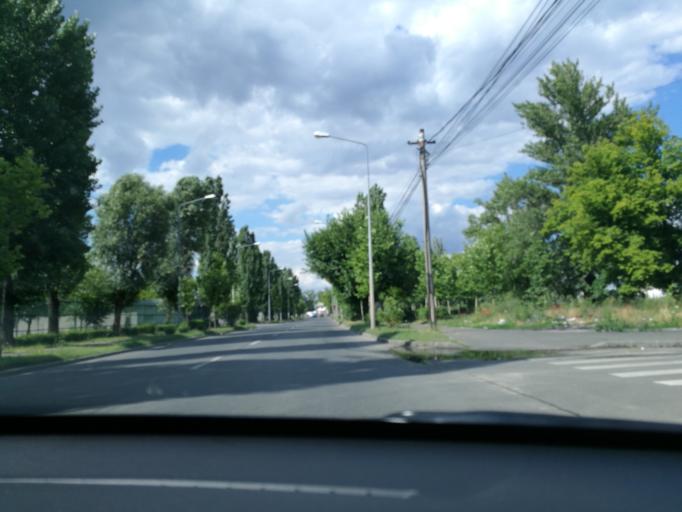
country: RO
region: Ilfov
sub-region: Comuna Glina
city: Catelu
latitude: 44.4232
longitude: 26.2197
